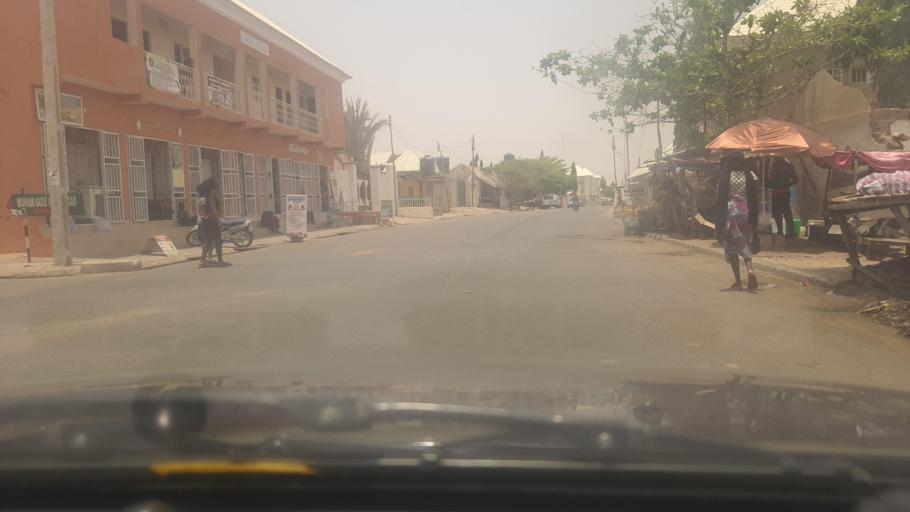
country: NG
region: Gombe
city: Gombe
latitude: 10.3006
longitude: 11.1466
